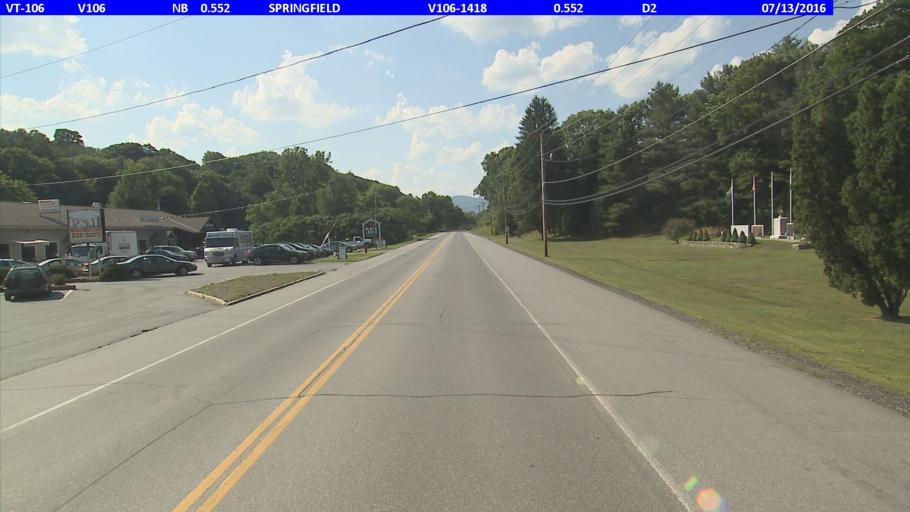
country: US
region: Vermont
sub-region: Windsor County
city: Springfield
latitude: 43.3098
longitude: -72.4977
